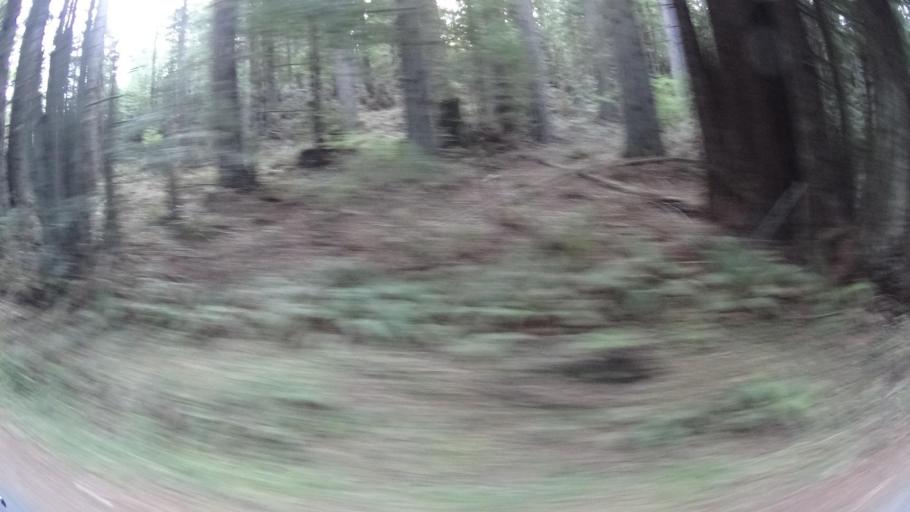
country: US
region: California
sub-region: Humboldt County
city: Bayside
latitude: 40.7567
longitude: -124.0016
